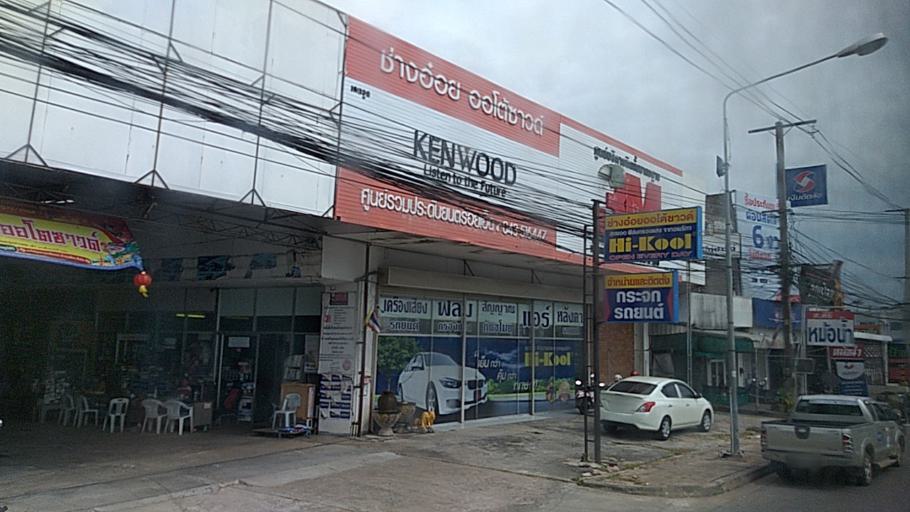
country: TH
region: Roi Et
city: Roi Et
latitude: 16.0560
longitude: 103.6382
